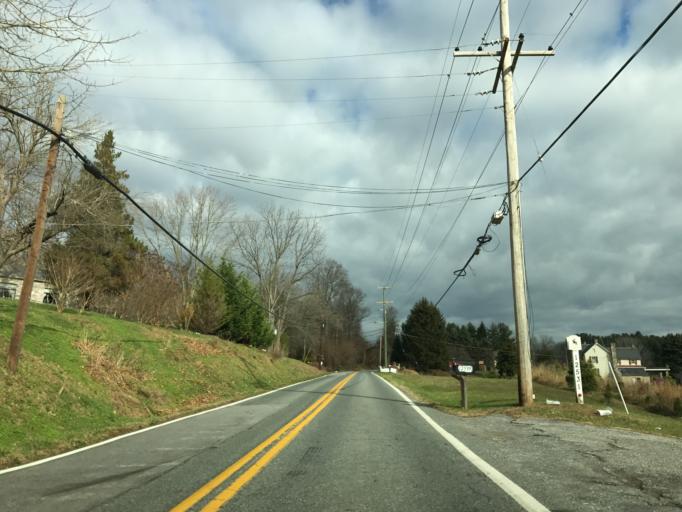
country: US
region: Maryland
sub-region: Baltimore County
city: Carney
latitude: 39.4681
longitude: -76.5257
